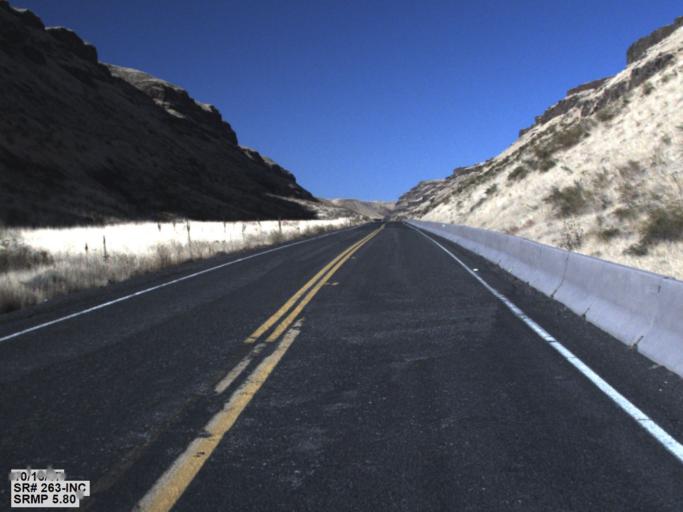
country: US
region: Washington
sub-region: Franklin County
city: Connell
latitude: 46.5983
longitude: -118.5487
